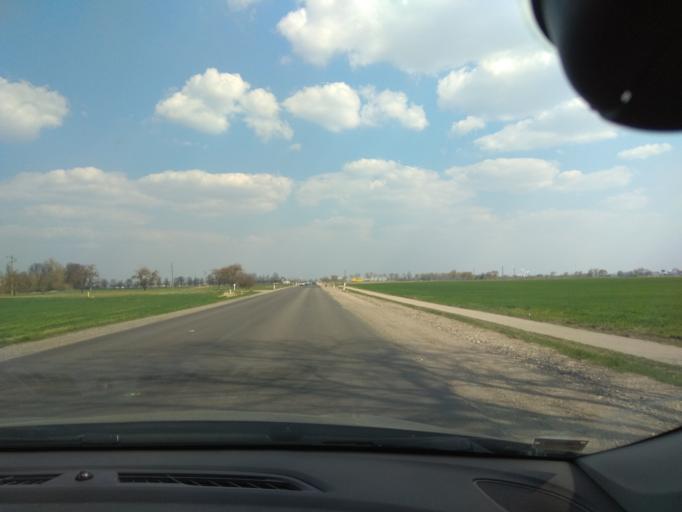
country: LT
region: Kauno apskritis
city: Kedainiai
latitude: 55.2682
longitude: 23.9163
